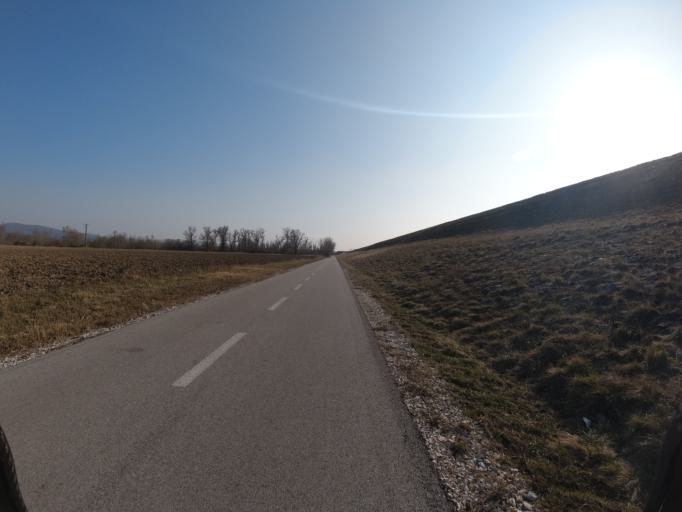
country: SK
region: Nitriansky
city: Cachtice
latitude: 48.6750
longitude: 17.8621
